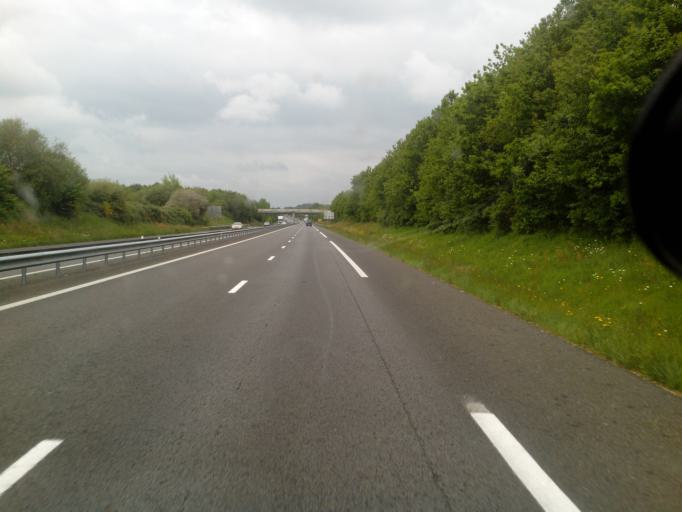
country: FR
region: Brittany
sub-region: Departement d'Ille-et-Vilaine
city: Saint-Etienne-en-Cogles
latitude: 48.3782
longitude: -1.3035
